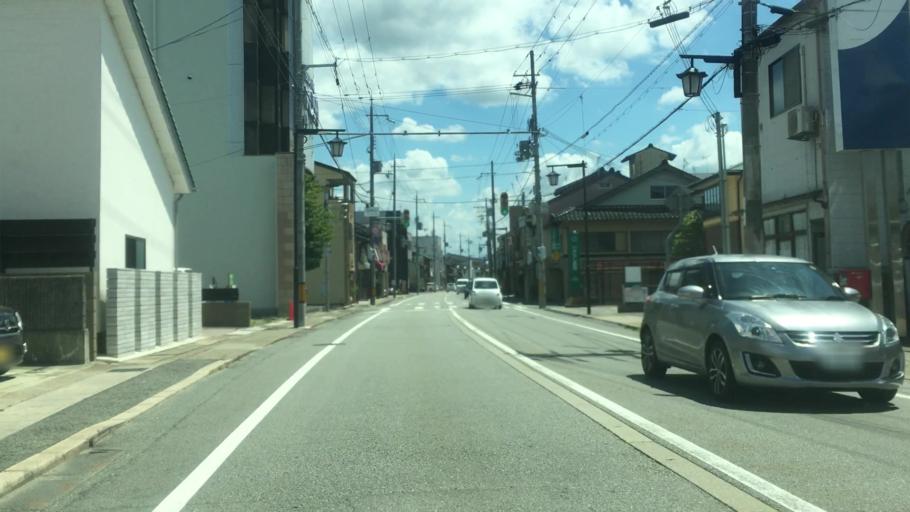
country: JP
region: Hyogo
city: Toyooka
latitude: 35.5387
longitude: 134.8245
